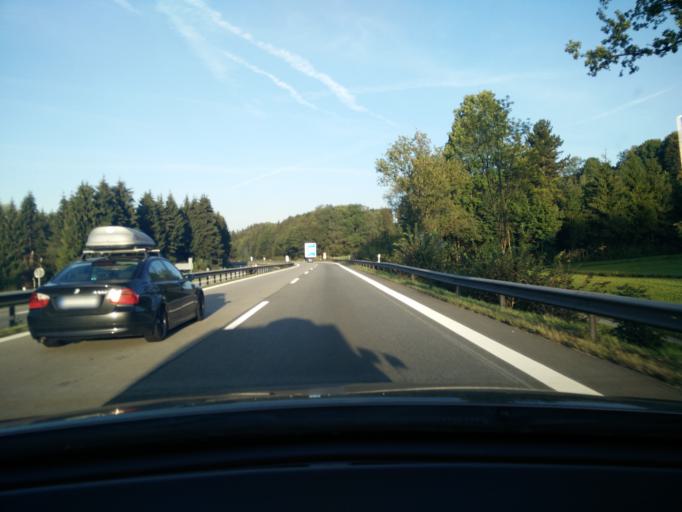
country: DE
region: Bavaria
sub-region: Upper Bavaria
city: Samerberg
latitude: 47.7967
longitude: 12.2146
